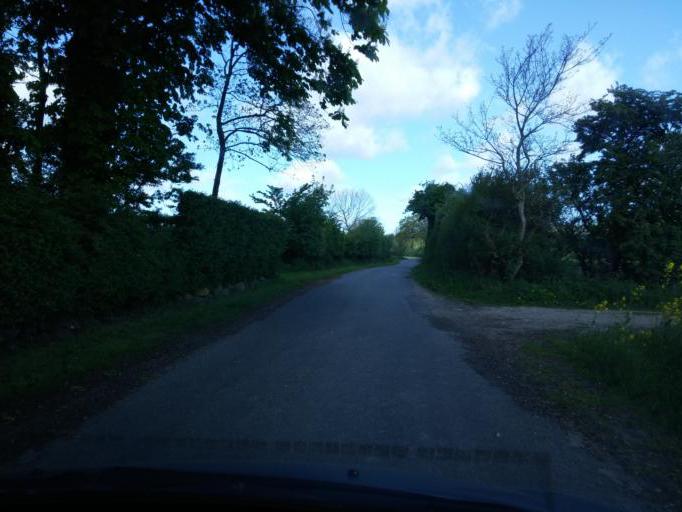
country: DK
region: South Denmark
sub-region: Kerteminde Kommune
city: Munkebo
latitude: 55.4112
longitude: 10.5441
